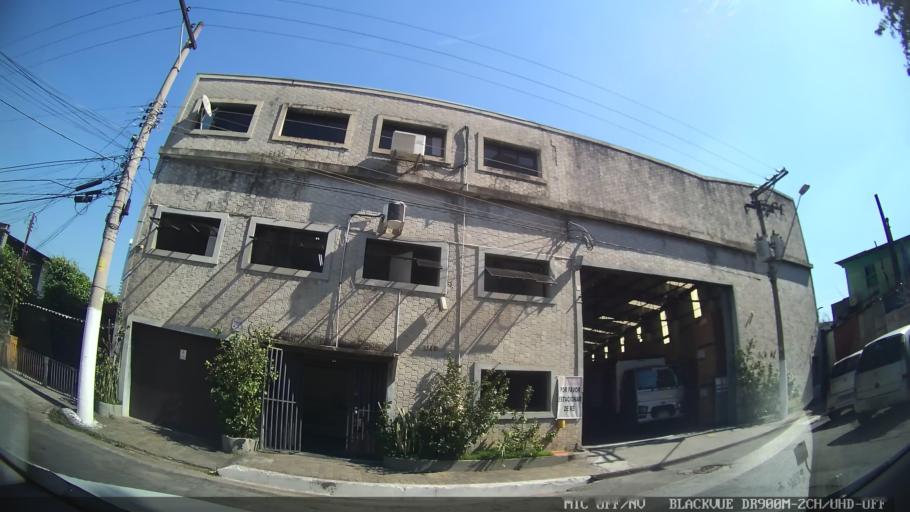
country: BR
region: Sao Paulo
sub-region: Sao Paulo
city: Sao Paulo
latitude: -23.5129
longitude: -46.6642
